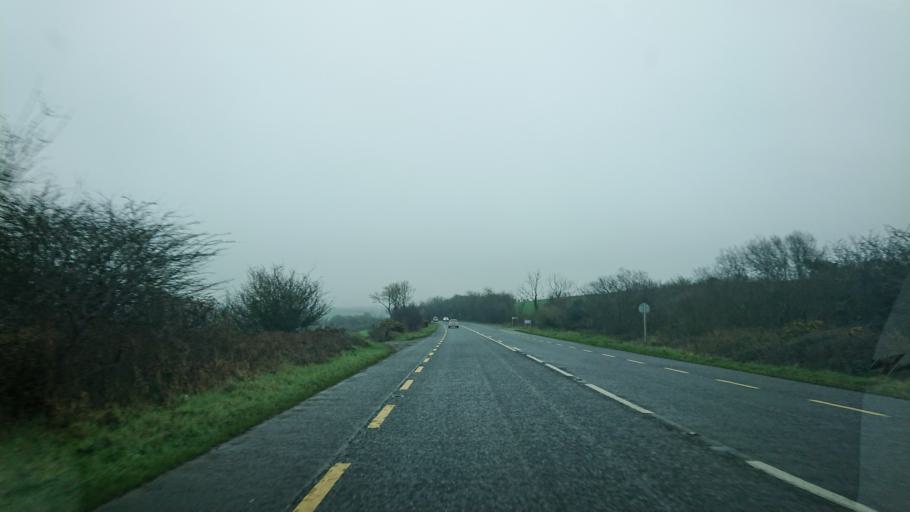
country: IE
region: Munster
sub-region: County Cork
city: Killumney
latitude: 51.7861
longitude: -8.6237
